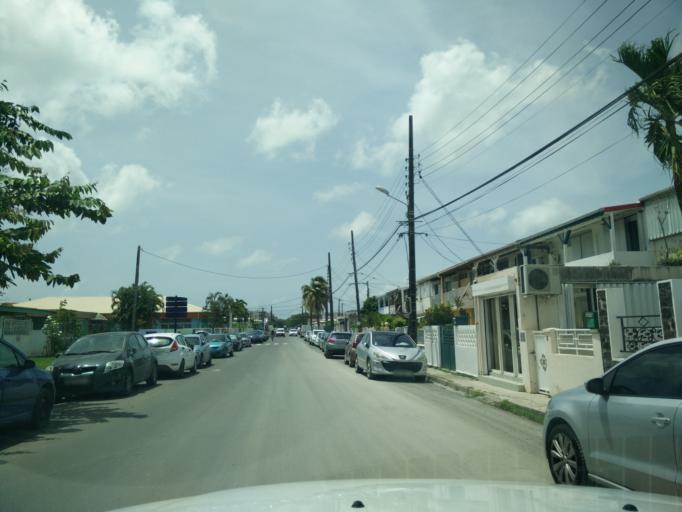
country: GP
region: Guadeloupe
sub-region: Guadeloupe
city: Pointe-a-Pitre
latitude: 16.2599
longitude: -61.5292
